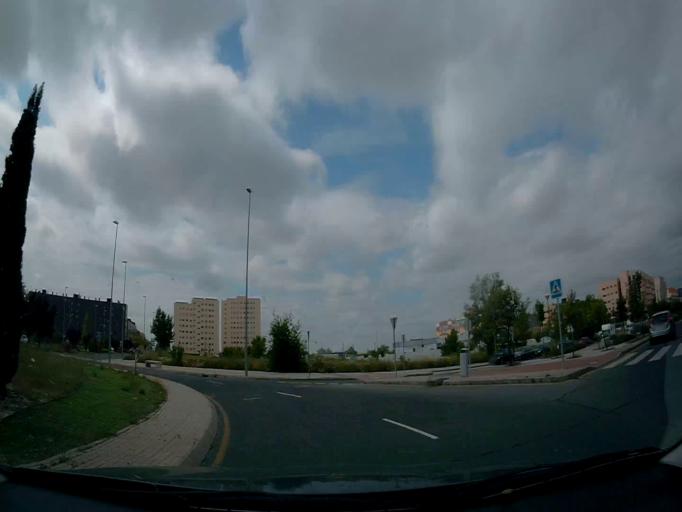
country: ES
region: Madrid
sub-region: Provincia de Madrid
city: Alcorcon
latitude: 40.3309
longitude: -3.8350
